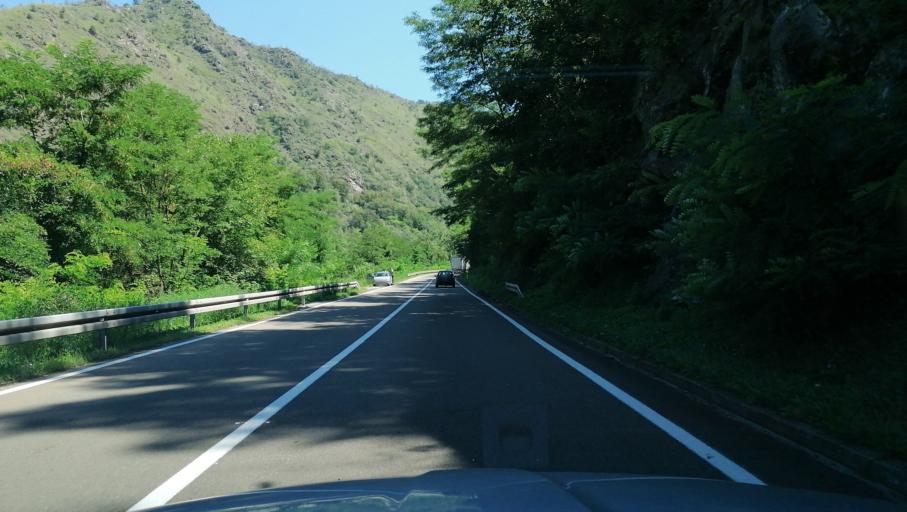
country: RS
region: Central Serbia
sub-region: Raski Okrug
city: Kraljevo
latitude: 43.5685
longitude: 20.5978
